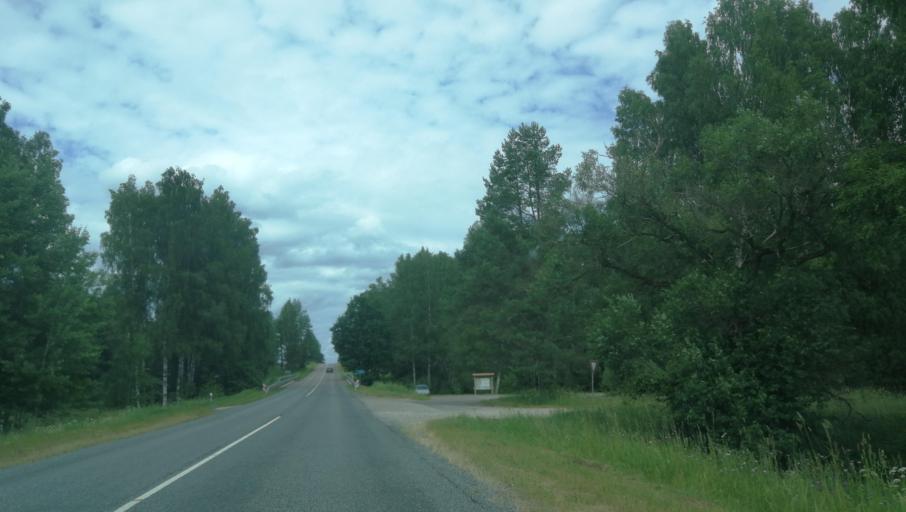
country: LV
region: Naukseni
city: Naukseni
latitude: 57.7859
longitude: 25.4247
